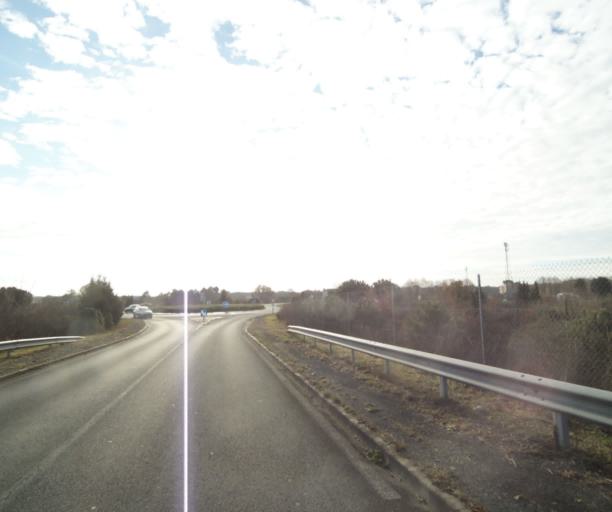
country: FR
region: Poitou-Charentes
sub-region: Departement de la Charente-Maritime
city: Saint-Romain-de-Benet
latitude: 45.6887
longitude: -0.8351
